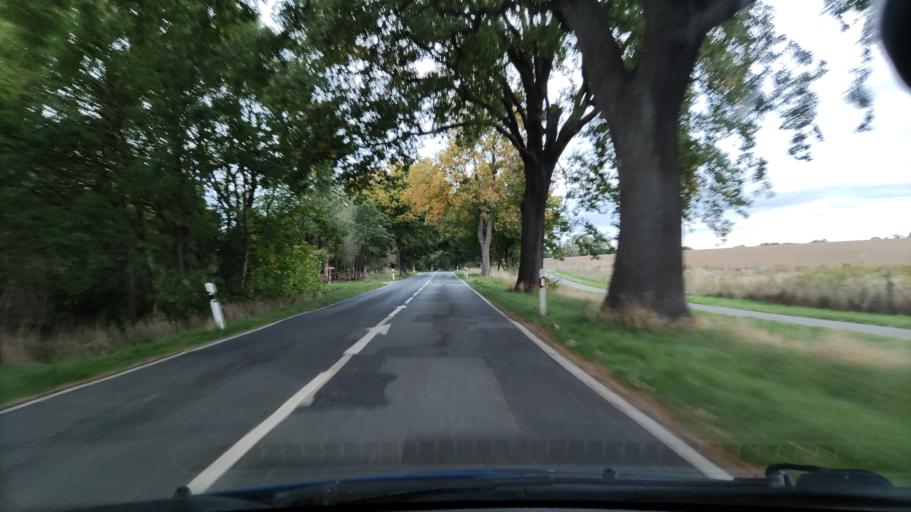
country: DE
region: Mecklenburg-Vorpommern
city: Lubtheen
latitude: 53.3887
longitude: 10.9661
